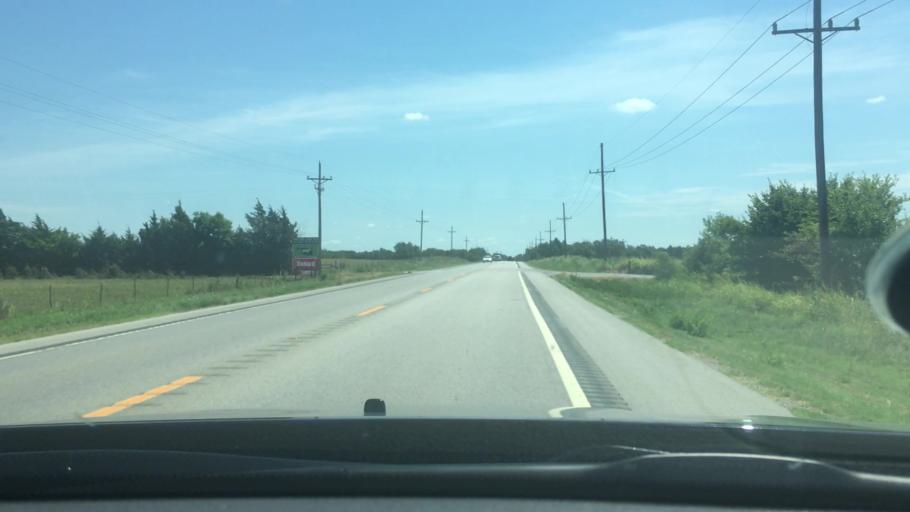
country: US
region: Oklahoma
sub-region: Bryan County
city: Durant
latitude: 33.9975
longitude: -96.2694
